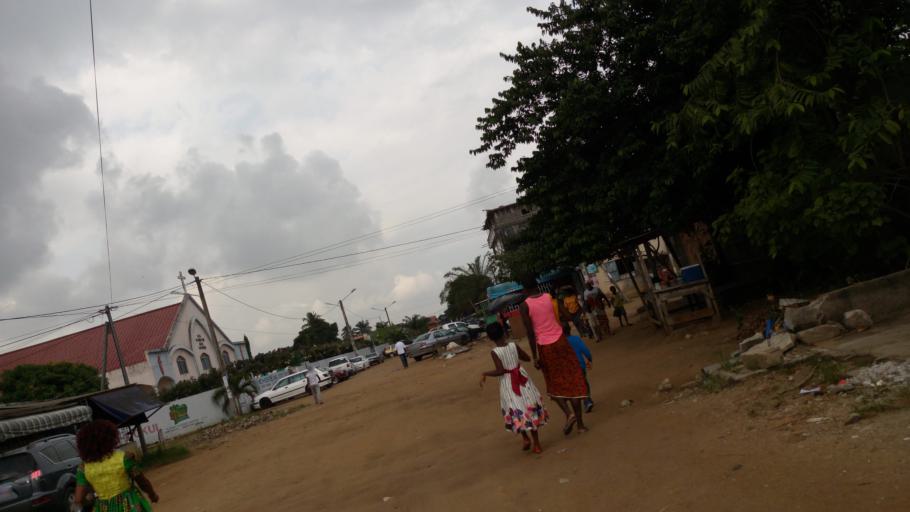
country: CI
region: Lagunes
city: Abobo
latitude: 5.3991
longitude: -4.0044
